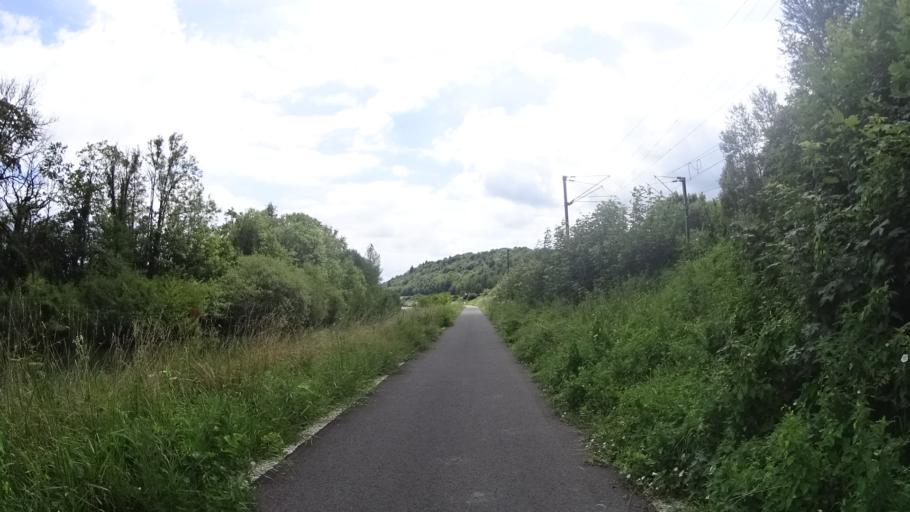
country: FR
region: Lorraine
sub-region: Departement de la Meuse
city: Commercy
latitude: 48.7773
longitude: 5.5686
